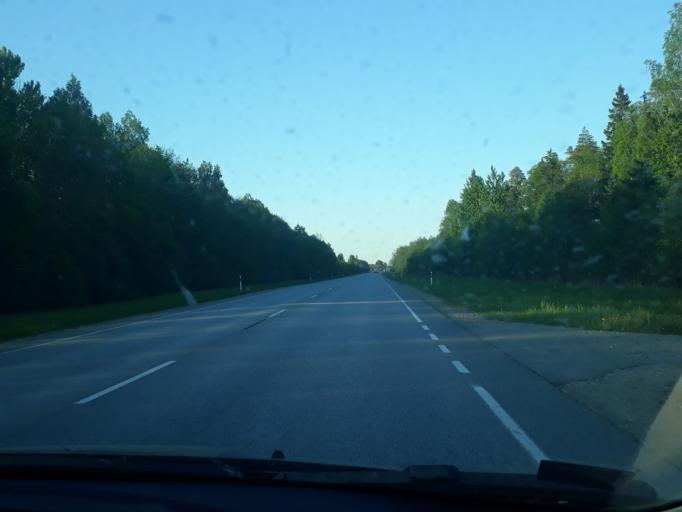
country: EE
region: Paernumaa
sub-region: Sindi linn
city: Sindi
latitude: 58.4699
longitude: 24.7125
